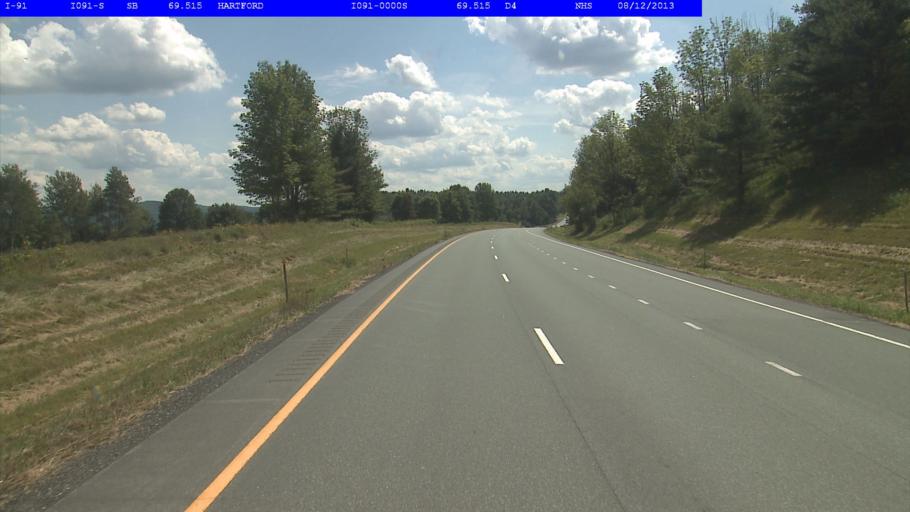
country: US
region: Vermont
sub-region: Windsor County
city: White River Junction
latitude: 43.6356
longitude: -72.3390
